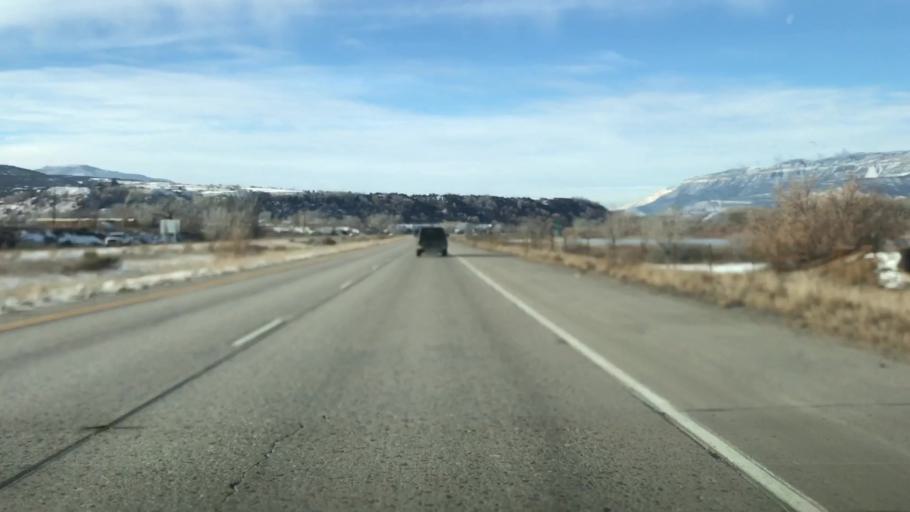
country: US
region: Colorado
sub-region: Garfield County
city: Rifle
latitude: 39.5220
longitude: -107.7850
